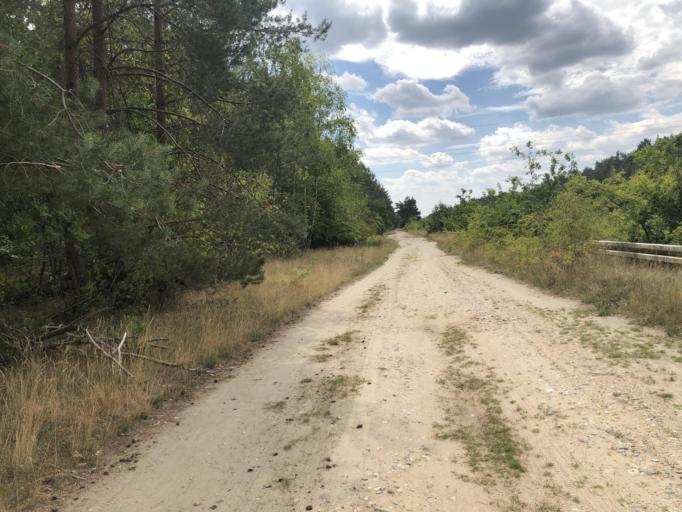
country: DE
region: Lower Saxony
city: Wendisch Evern
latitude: 53.2093
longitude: 10.4964
